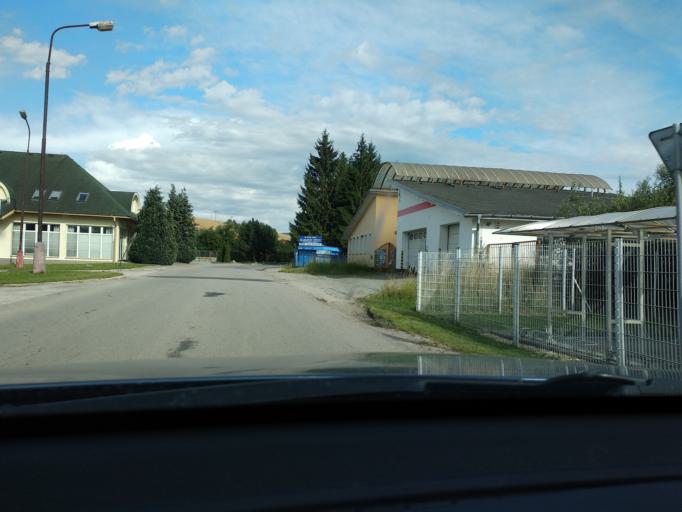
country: SK
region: Zilinsky
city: Ruzomberok
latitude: 49.0726
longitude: 19.3163
